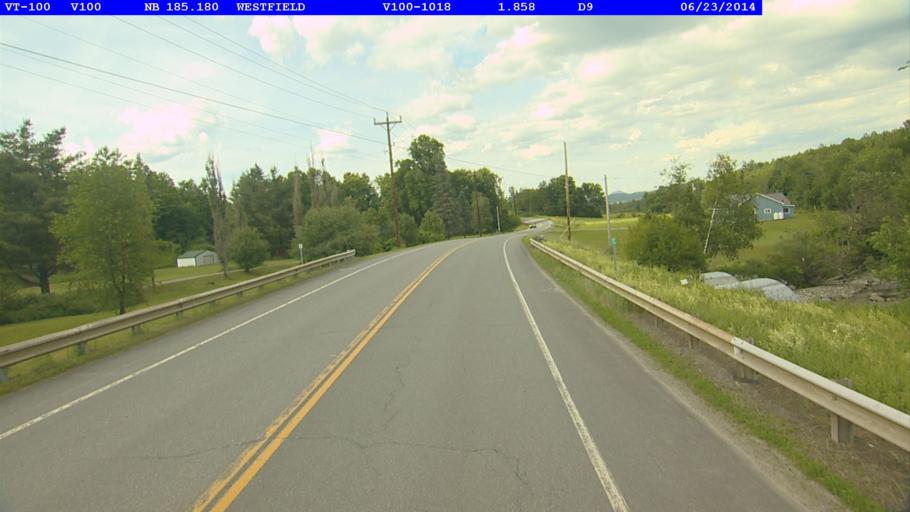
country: US
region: Vermont
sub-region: Orleans County
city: Newport
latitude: 44.8617
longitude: -72.4342
